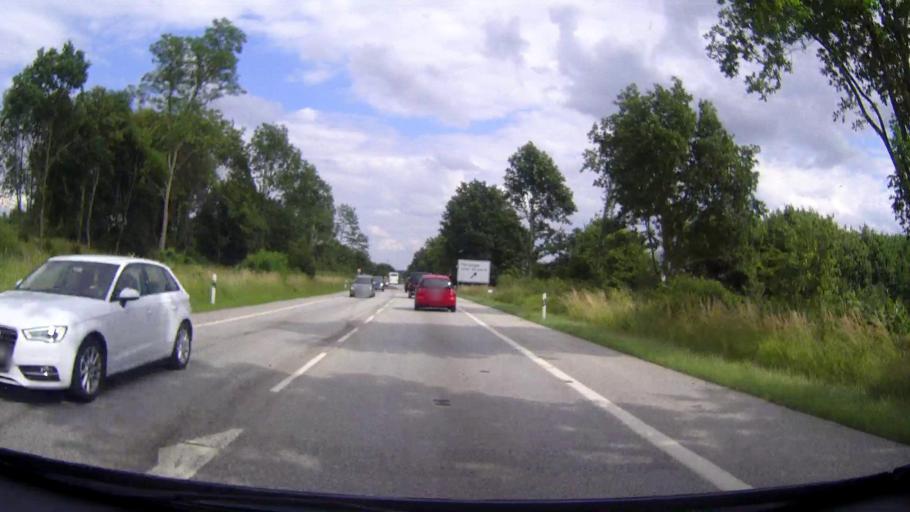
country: DE
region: Schleswig-Holstein
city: Klein Gladebrugge
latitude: 53.9245
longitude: 10.3270
